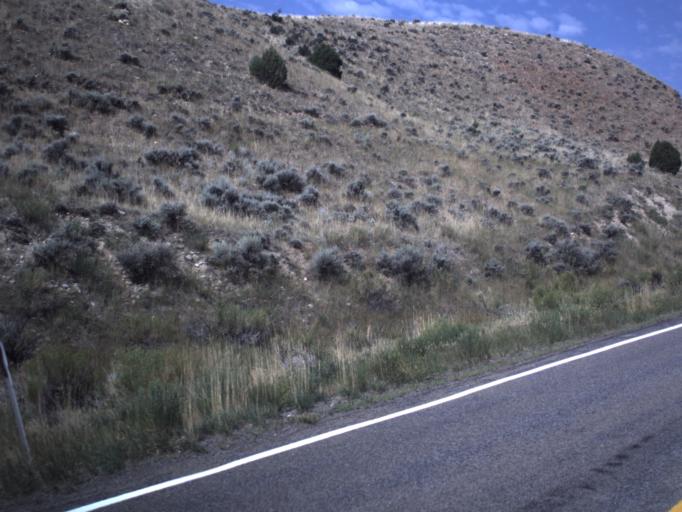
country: US
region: Utah
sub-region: Daggett County
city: Manila
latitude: 40.9232
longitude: -109.7085
